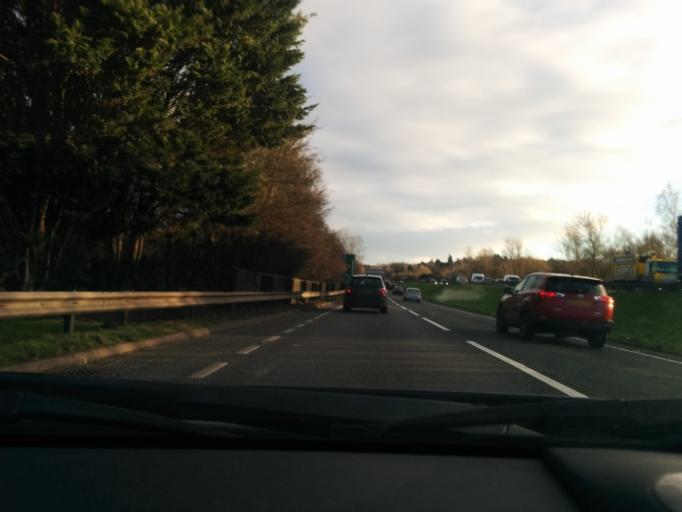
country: GB
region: England
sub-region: Oxfordshire
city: Oxford
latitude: 51.7340
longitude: -1.2677
